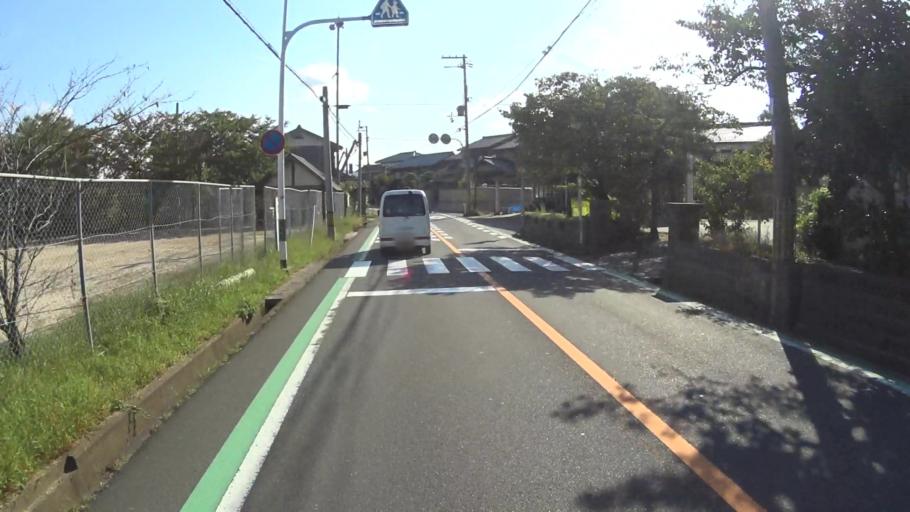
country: JP
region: Kyoto
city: Miyazu
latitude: 35.6918
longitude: 135.0355
